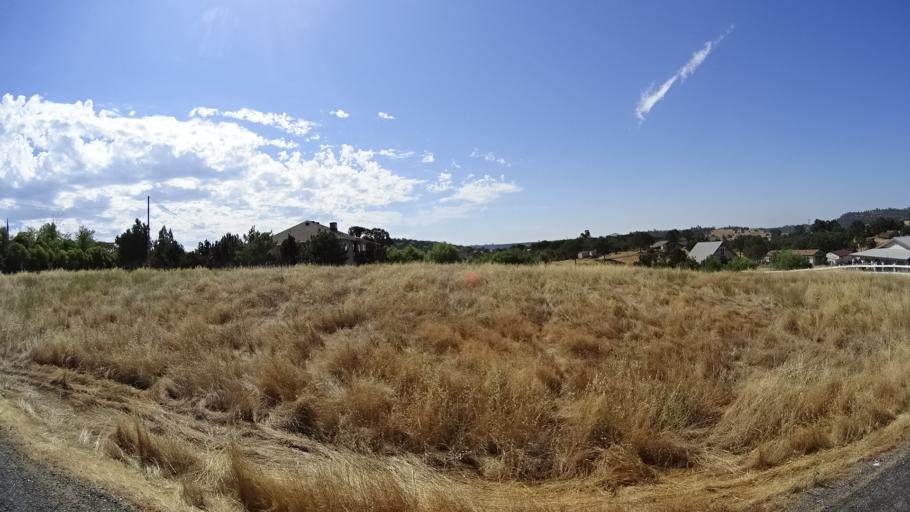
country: US
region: California
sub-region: Calaveras County
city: Copperopolis
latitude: 37.9172
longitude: -120.6233
